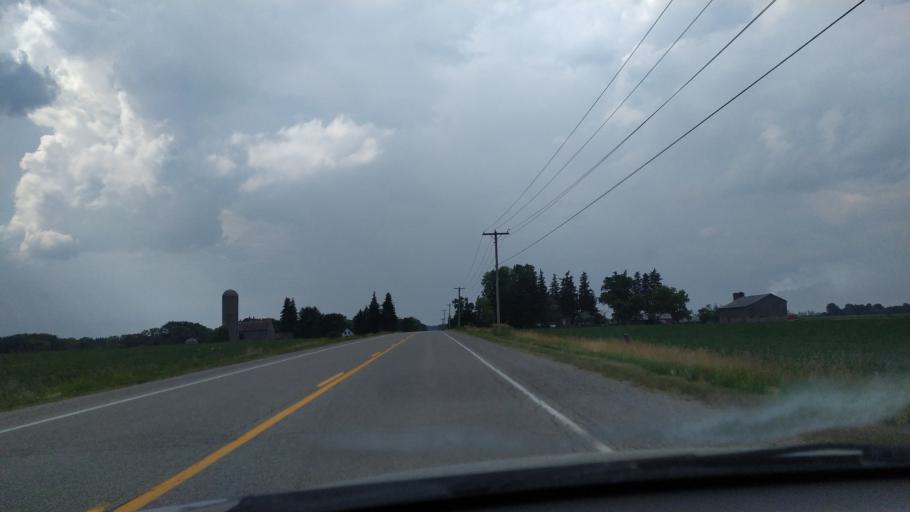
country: CA
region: Ontario
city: London
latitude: 43.2049
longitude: -81.1551
